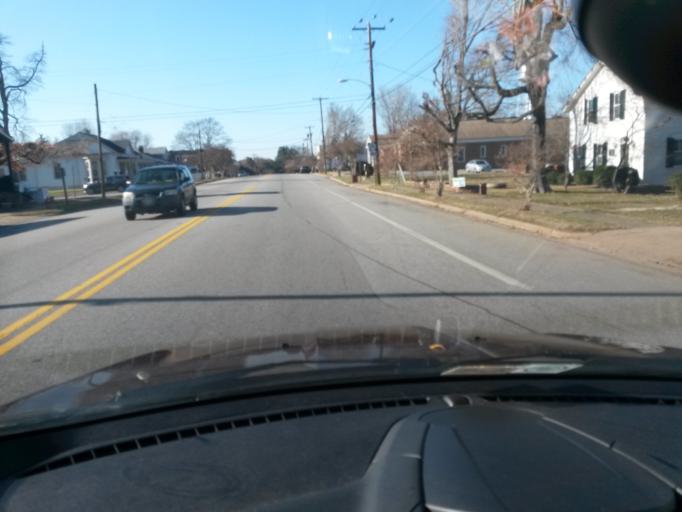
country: US
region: Virginia
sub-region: Charlotte County
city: Charlotte Court House
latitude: 37.0398
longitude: -78.4817
